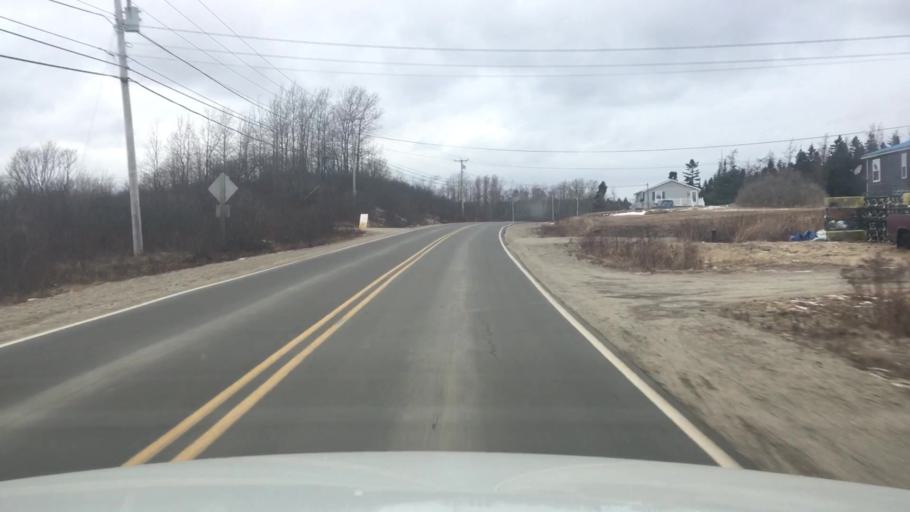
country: US
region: Maine
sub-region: Washington County
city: Jonesport
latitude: 44.5516
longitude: -67.6227
